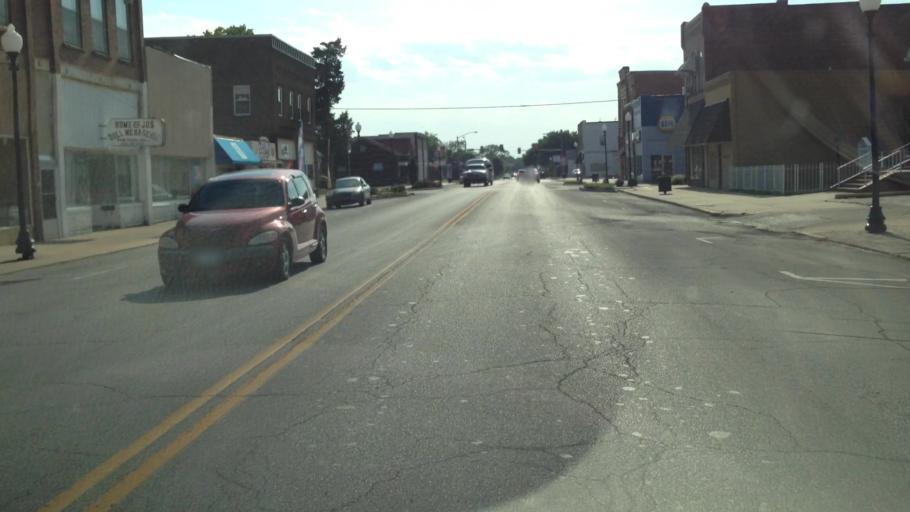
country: US
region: Kansas
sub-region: Wilson County
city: Neodesha
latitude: 37.4176
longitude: -95.6815
